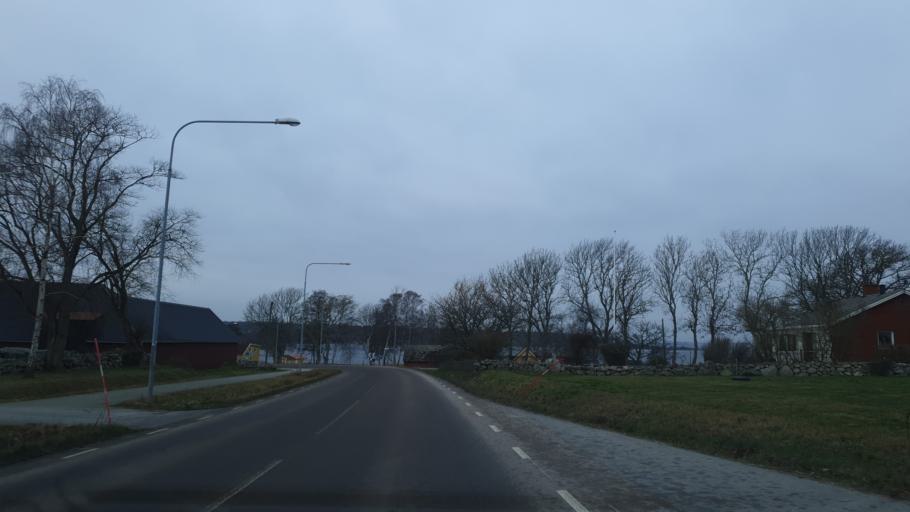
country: SE
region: Blekinge
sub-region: Karlskrona Kommun
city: Sturko
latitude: 56.1144
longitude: 15.6900
